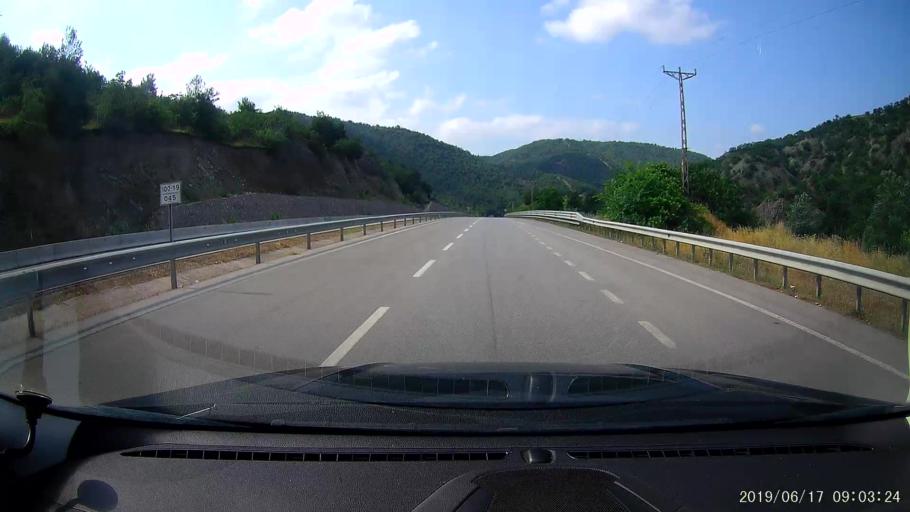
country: TR
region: Amasya
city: Tasova
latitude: 40.7560
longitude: 36.3023
